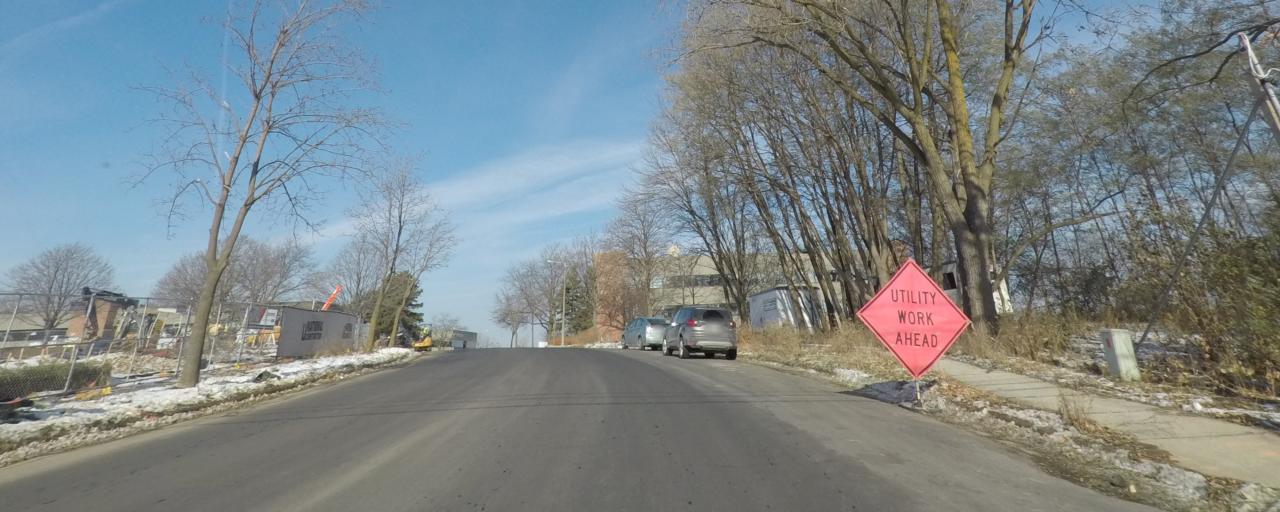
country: US
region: Wisconsin
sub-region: Dane County
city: Madison
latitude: 43.0314
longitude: -89.4146
